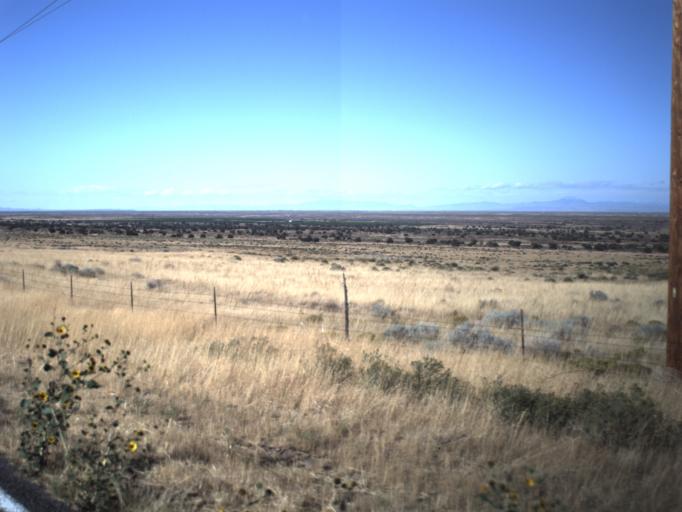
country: US
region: Utah
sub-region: Millard County
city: Delta
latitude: 39.4463
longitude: -112.3106
